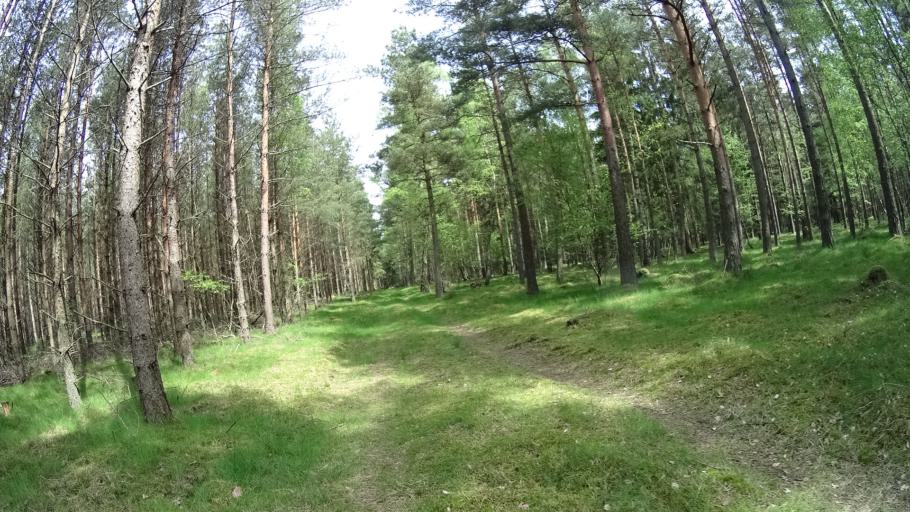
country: SE
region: Skane
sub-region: Sjobo Kommun
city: Sjoebo
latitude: 55.6713
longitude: 13.6365
